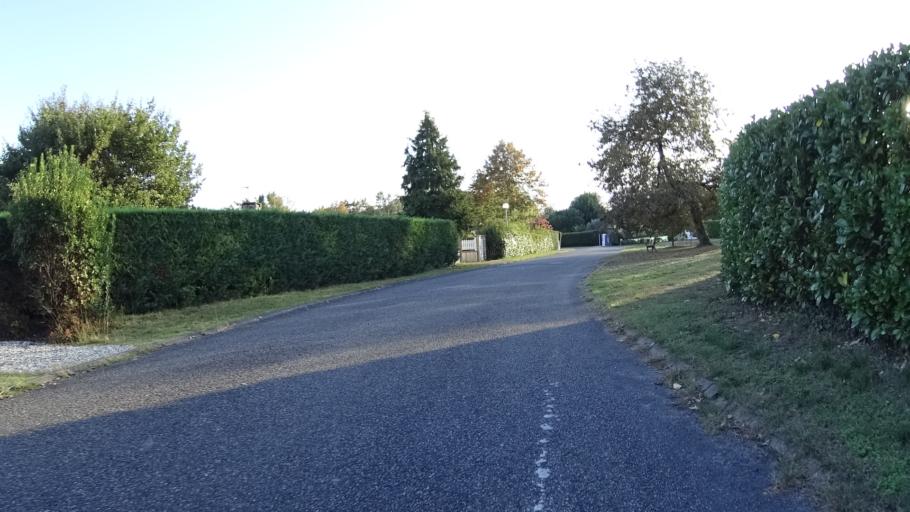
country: FR
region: Aquitaine
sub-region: Departement des Landes
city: Saint-Paul-les-Dax
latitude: 43.7392
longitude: -1.0476
